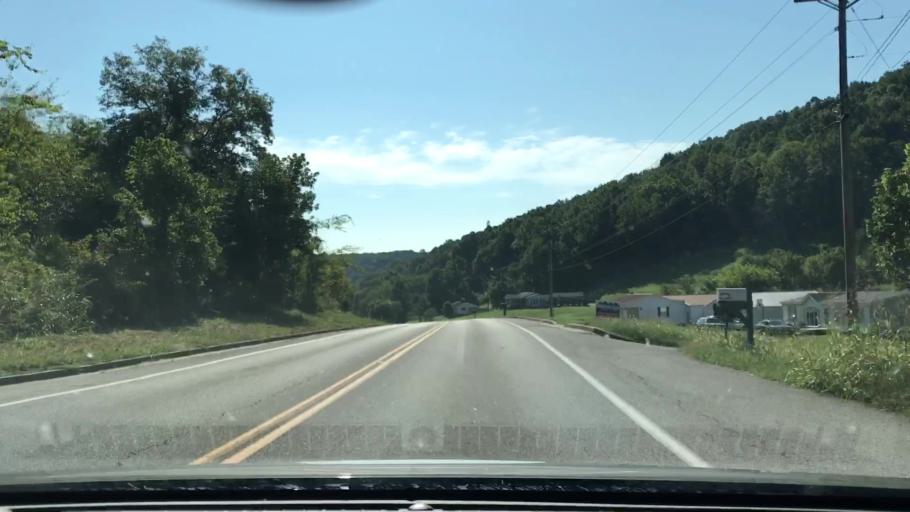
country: US
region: Tennessee
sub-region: Smith County
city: Carthage
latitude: 36.3218
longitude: -85.9244
